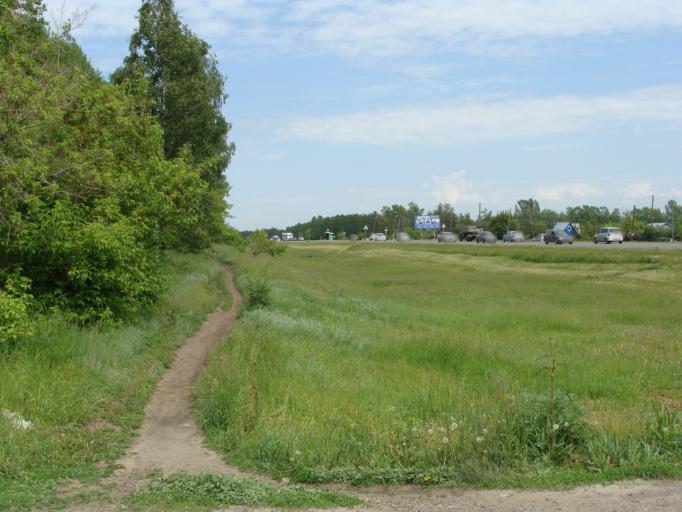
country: RU
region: Altai Krai
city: Yuzhnyy
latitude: 53.2372
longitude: 83.6956
